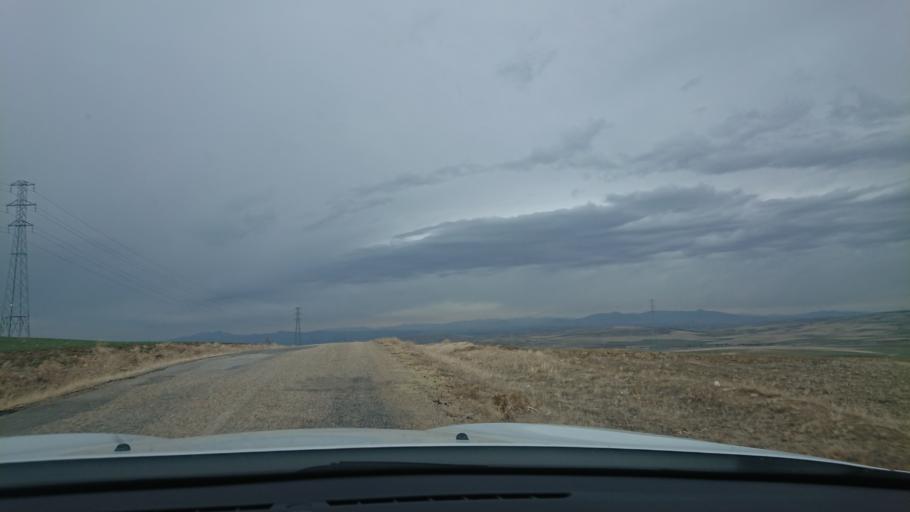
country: TR
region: Aksaray
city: Agacoren
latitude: 38.9366
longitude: 33.9154
